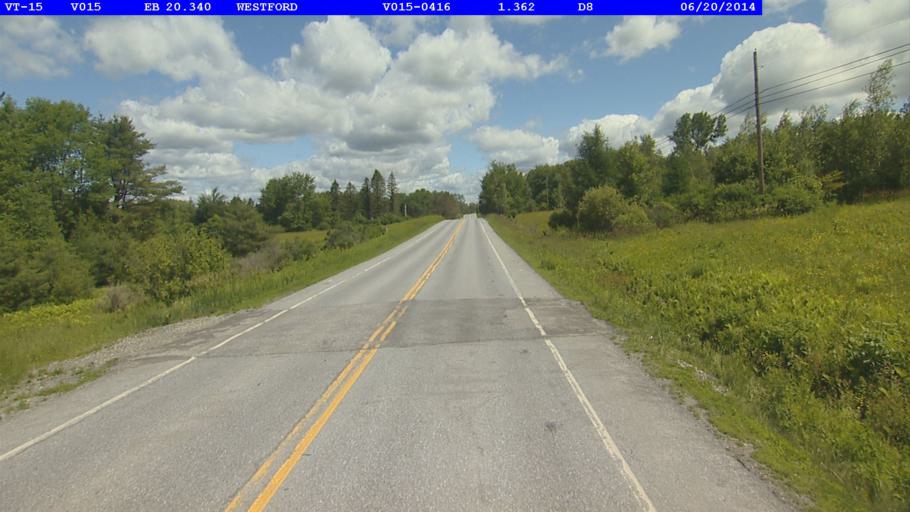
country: US
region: Vermont
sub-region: Chittenden County
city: Jericho
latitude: 44.6132
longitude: -72.9292
